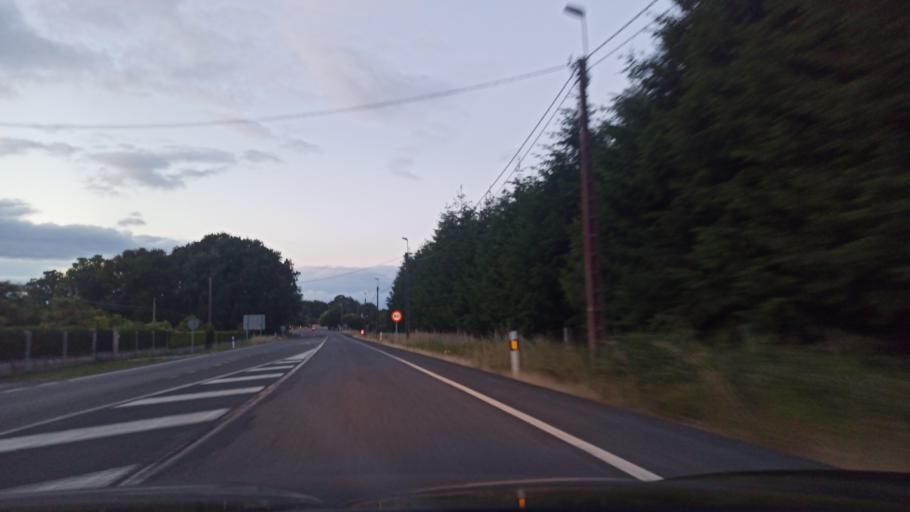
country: ES
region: Galicia
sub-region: Provincia de Lugo
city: Lugo
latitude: 42.9615
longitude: -7.6014
